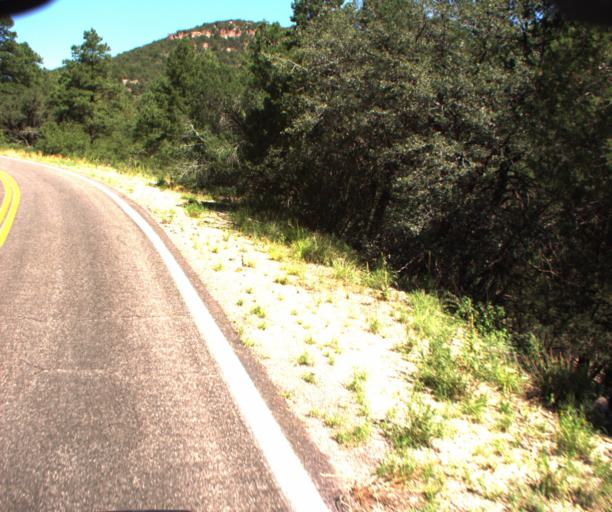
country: US
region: Arizona
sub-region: Greenlee County
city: Morenci
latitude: 33.1782
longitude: -109.3752
